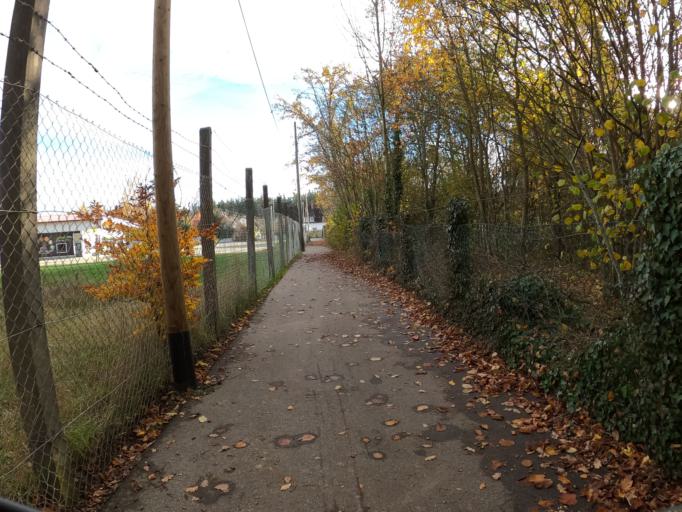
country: DE
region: Bavaria
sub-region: Swabia
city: Nersingen
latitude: 48.4136
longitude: 10.1532
